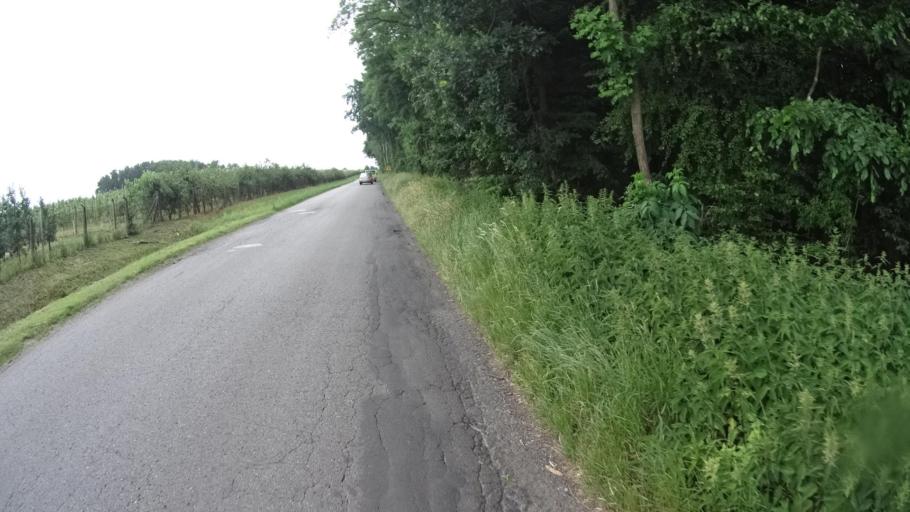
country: PL
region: Masovian Voivodeship
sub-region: Powiat grojecki
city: Goszczyn
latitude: 51.7781
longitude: 20.8535
